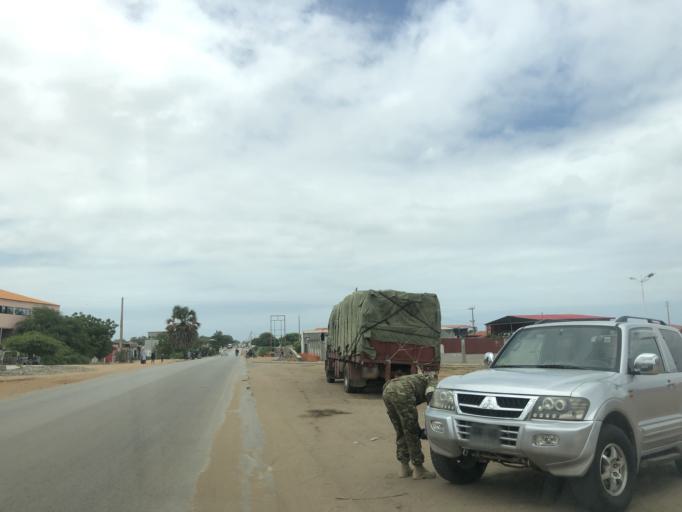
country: AO
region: Luanda
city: Luanda
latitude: -9.0607
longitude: 13.0455
